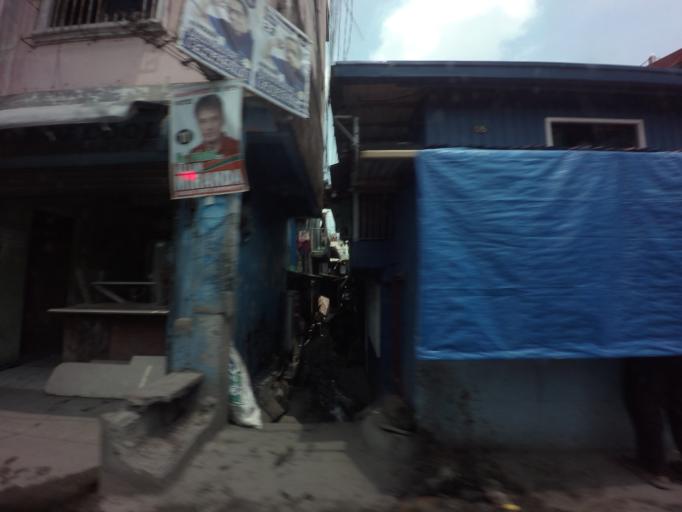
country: PH
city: Sambayanihan People's Village
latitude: 14.4368
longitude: 121.0502
